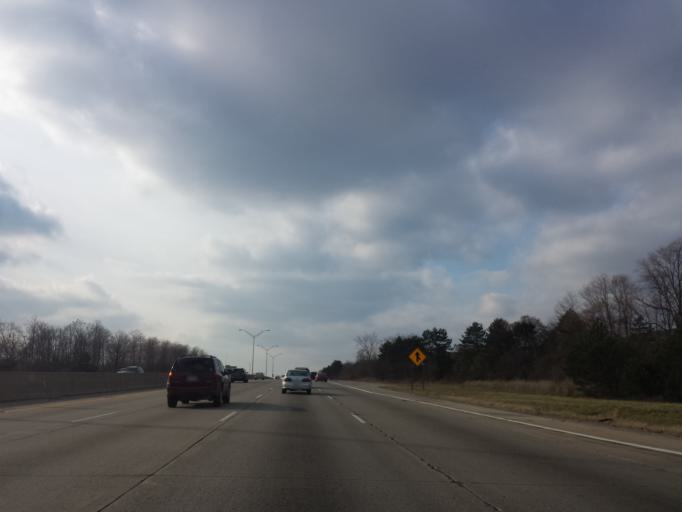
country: US
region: Michigan
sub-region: Oakland County
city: Farmington Hills
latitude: 42.4961
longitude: -83.3613
